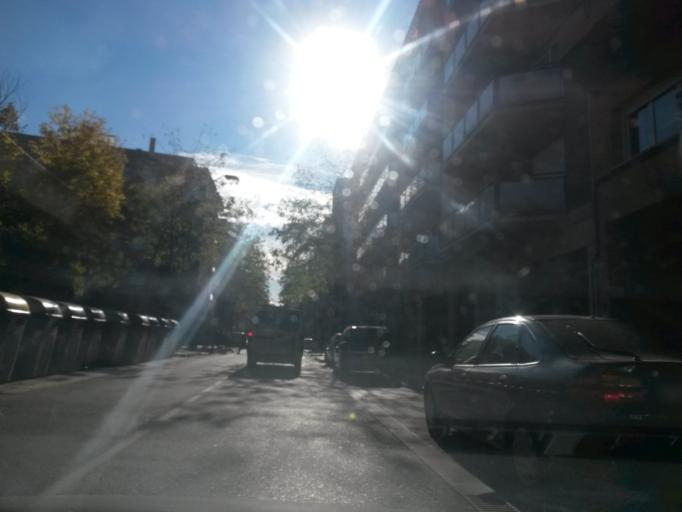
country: ES
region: Catalonia
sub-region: Provincia de Girona
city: Salt
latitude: 41.9761
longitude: 2.8026
